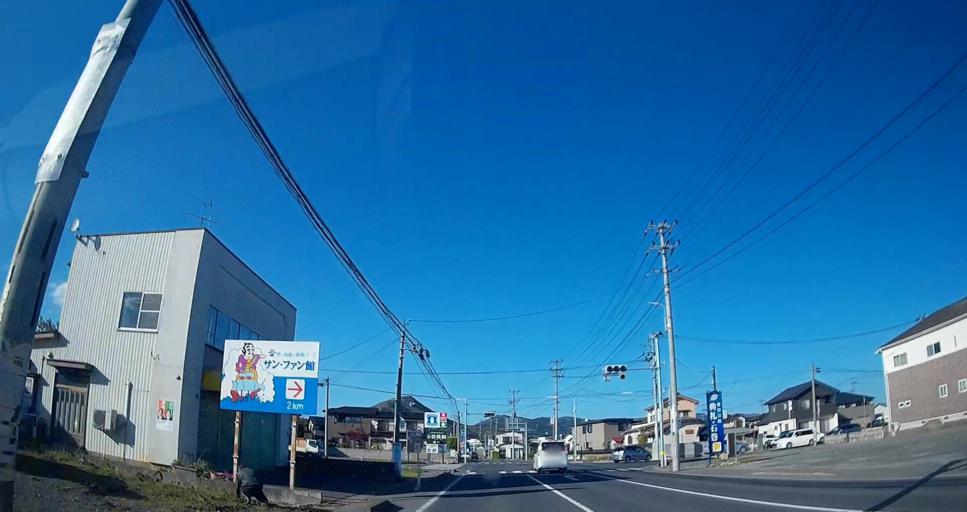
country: JP
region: Miyagi
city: Ishinomaki
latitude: 38.4186
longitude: 141.3662
